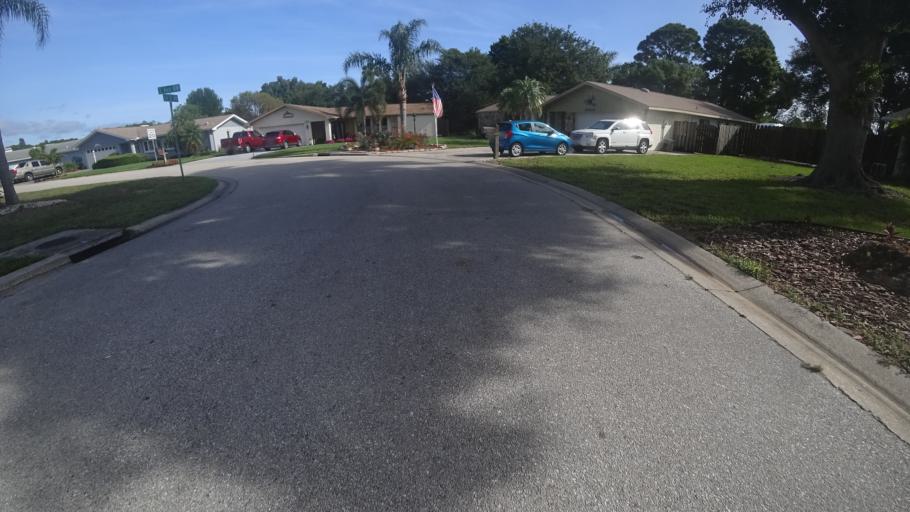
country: US
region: Florida
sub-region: Manatee County
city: West Bradenton
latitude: 27.5018
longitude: -82.6299
